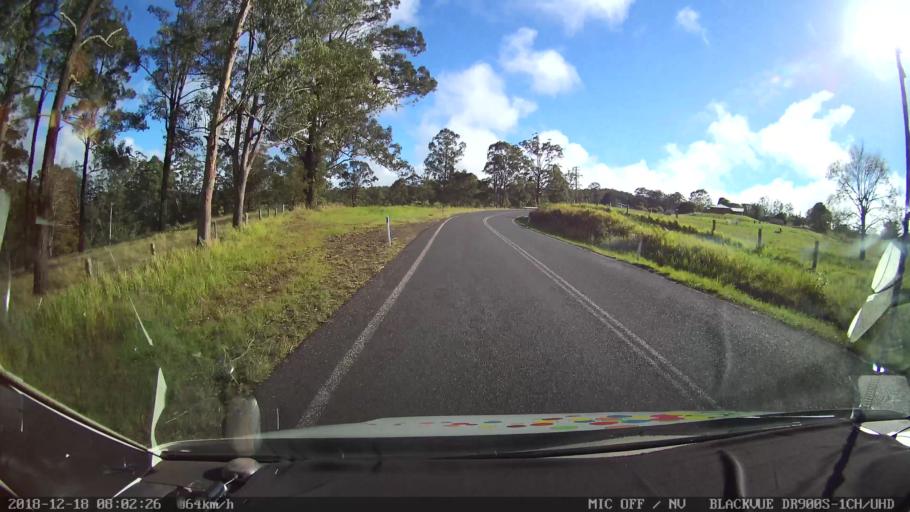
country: AU
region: New South Wales
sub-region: Kyogle
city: Kyogle
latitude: -28.3924
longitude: 152.6327
